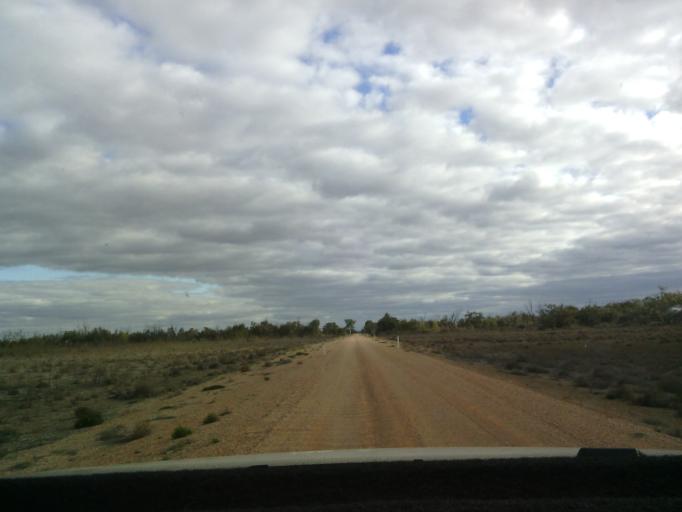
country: AU
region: South Australia
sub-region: Renmark Paringa
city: Renmark
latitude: -34.1644
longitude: 141.1947
